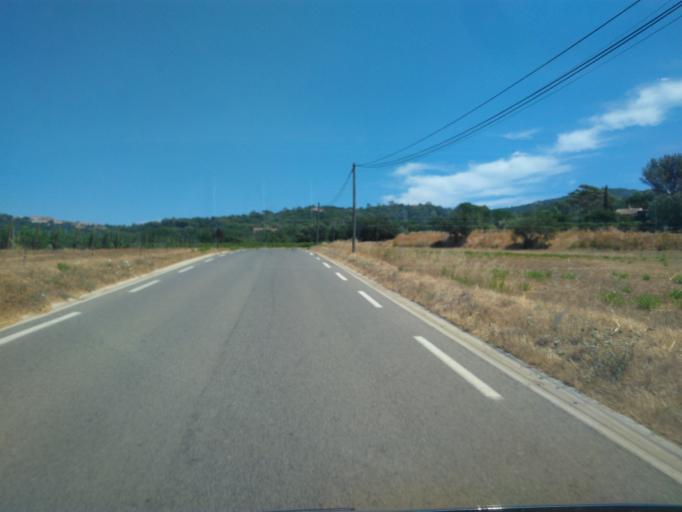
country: FR
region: Provence-Alpes-Cote d'Azur
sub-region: Departement du Var
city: Gassin
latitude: 43.2153
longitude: 6.5807
